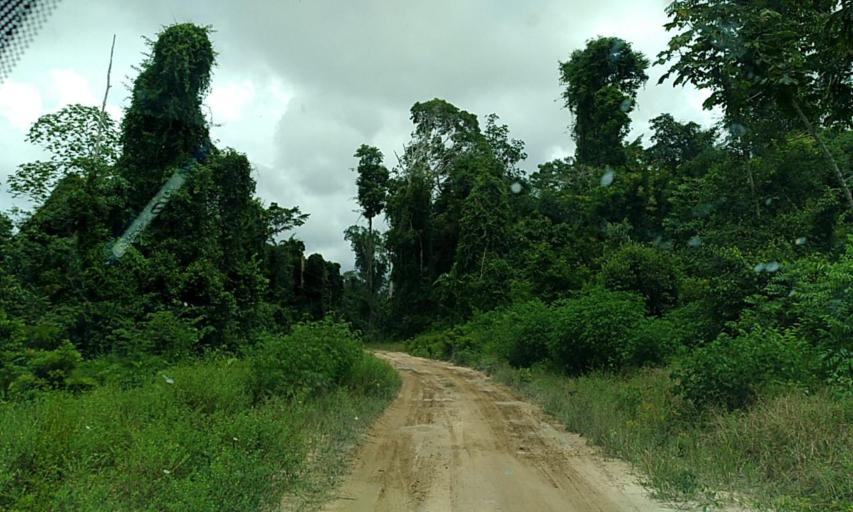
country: BR
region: Para
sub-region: Altamira
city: Altamira
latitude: -3.0511
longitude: -52.9086
